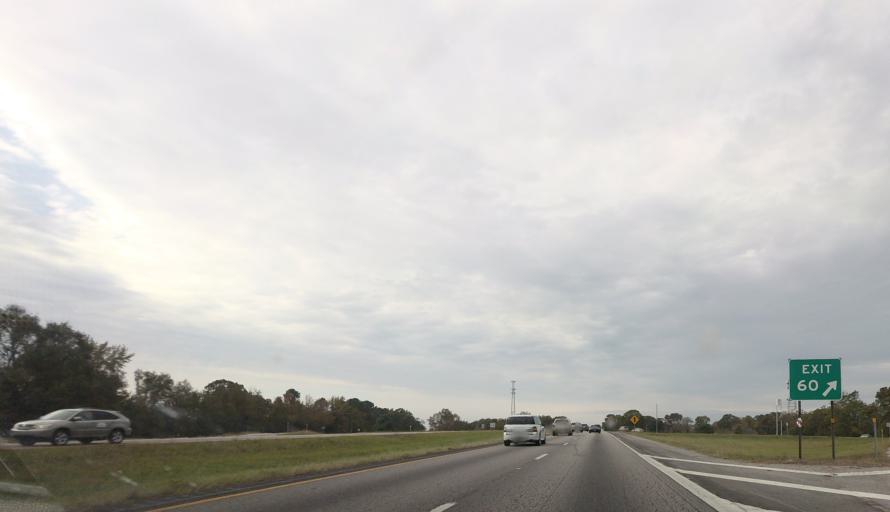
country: US
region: Alabama
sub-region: Lee County
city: Opelika
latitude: 32.6336
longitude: -85.3691
